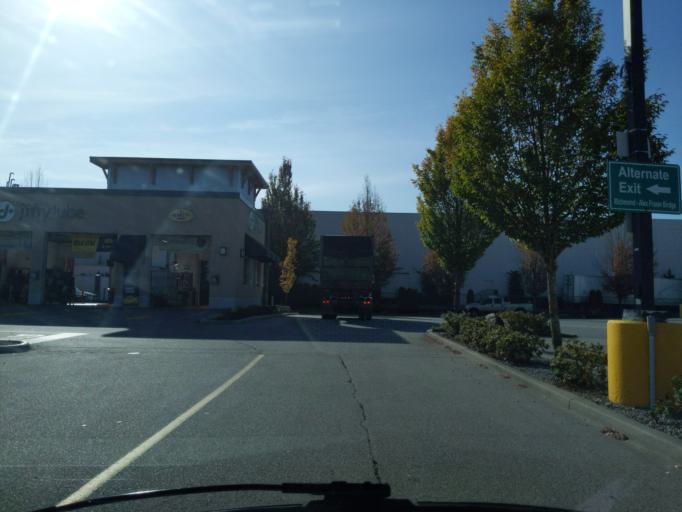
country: CA
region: British Columbia
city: New Westminster
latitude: 49.1909
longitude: -122.9503
